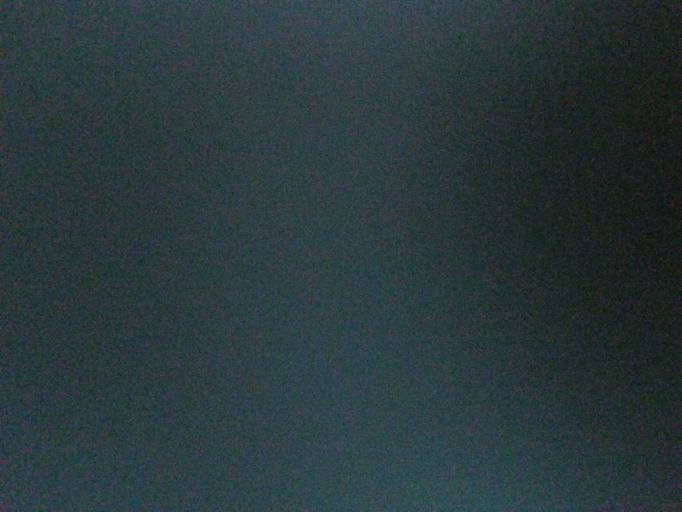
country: DE
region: Bavaria
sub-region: Upper Bavaria
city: Pasing
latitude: 48.1421
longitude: 11.5130
